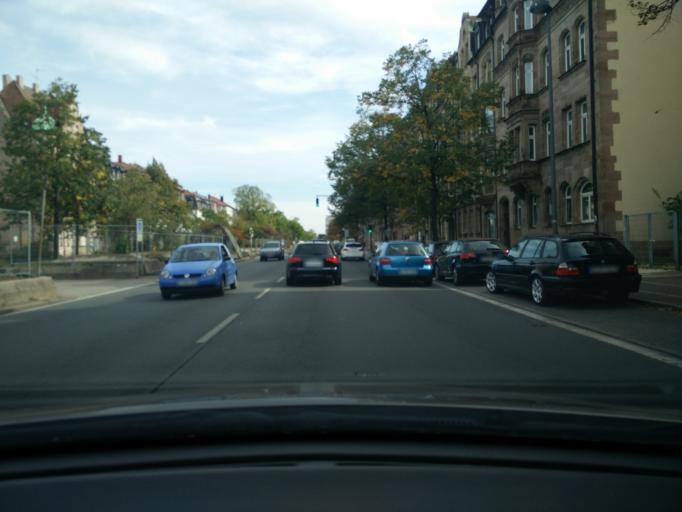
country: DE
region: Bavaria
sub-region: Regierungsbezirk Mittelfranken
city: Wetzendorf
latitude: 49.4527
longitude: 11.0500
